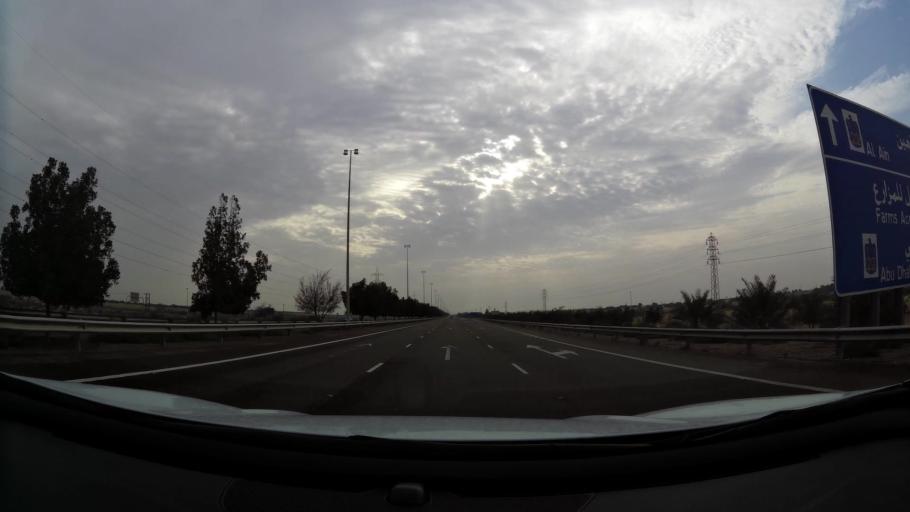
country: AE
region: Abu Dhabi
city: Abu Dhabi
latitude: 24.2026
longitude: 54.9056
